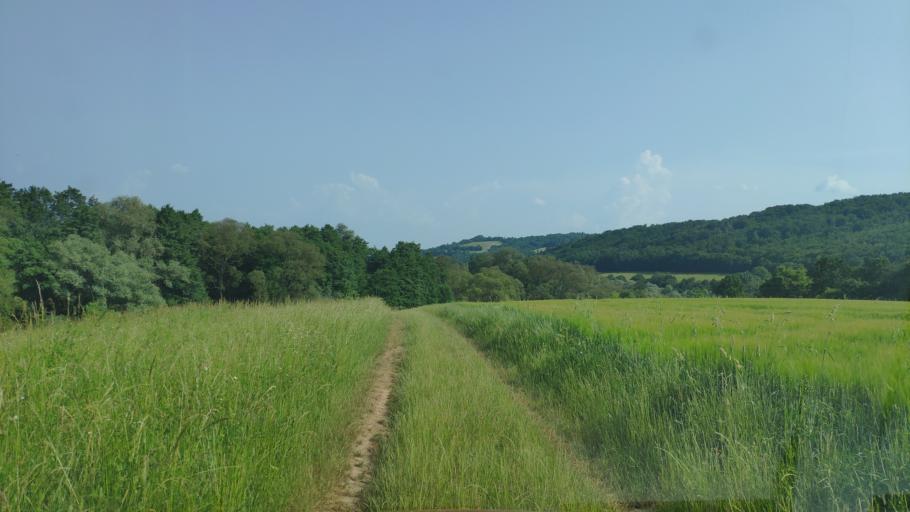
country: SK
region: Presovsky
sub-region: Okres Presov
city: Presov
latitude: 48.9566
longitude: 21.1557
